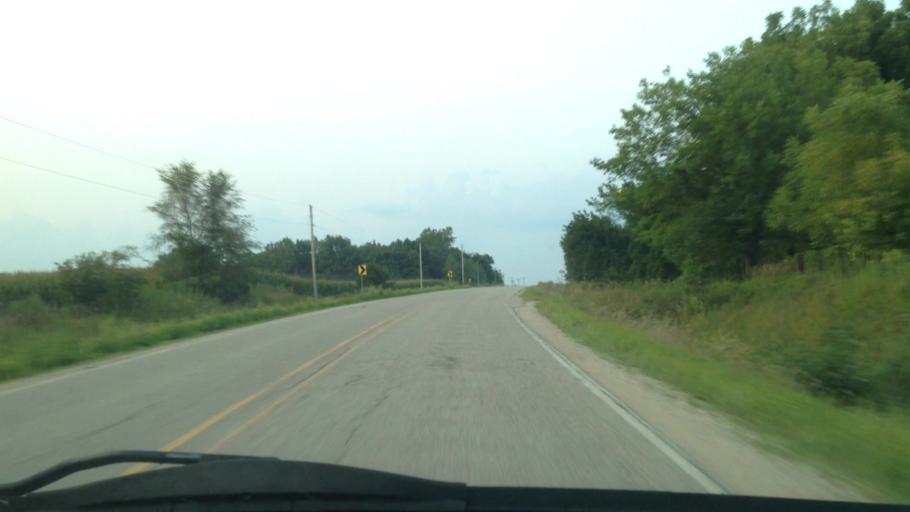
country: US
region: Iowa
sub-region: Benton County
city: Urbana
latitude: 42.1574
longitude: -91.8770
